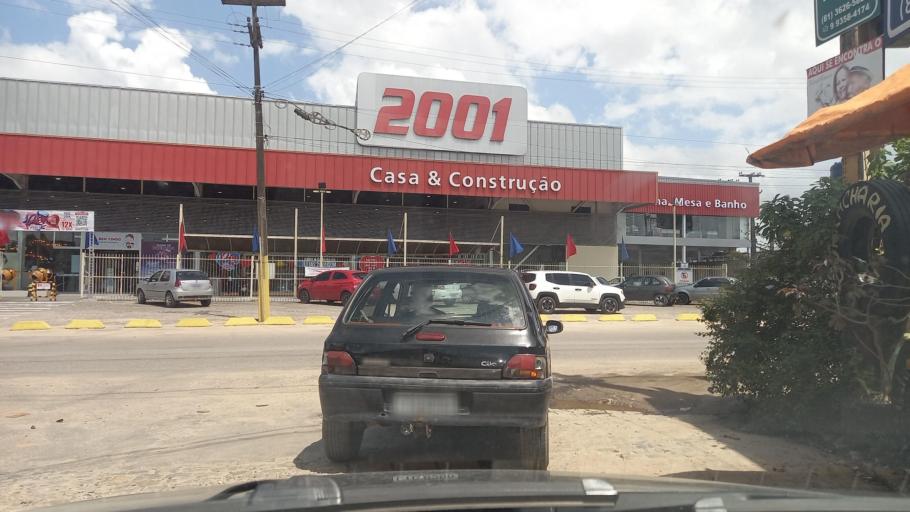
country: BR
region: Pernambuco
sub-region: Goiana
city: Goiana
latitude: -7.5661
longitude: -34.9942
